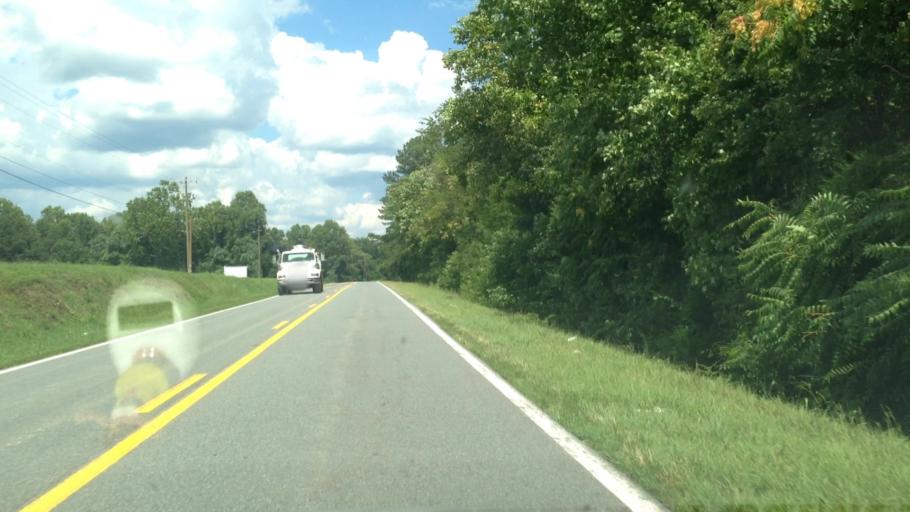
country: US
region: North Carolina
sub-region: Rockingham County
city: Reidsville
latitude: 36.4122
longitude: -79.6103
